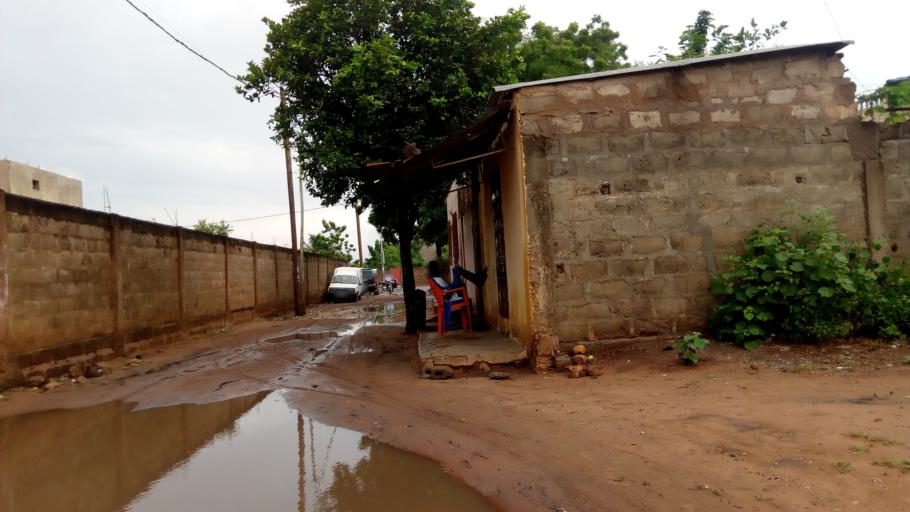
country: TG
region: Maritime
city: Lome
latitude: 6.2155
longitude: 1.1734
